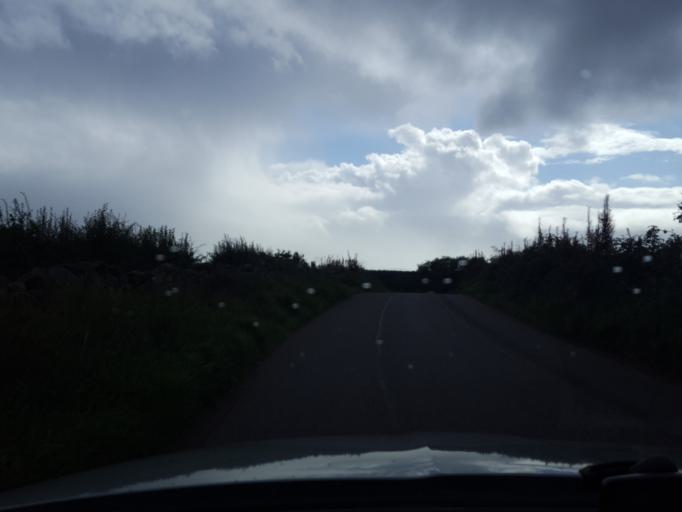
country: GB
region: Scotland
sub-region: Aberdeenshire
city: Banchory
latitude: 57.0893
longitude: -2.4483
